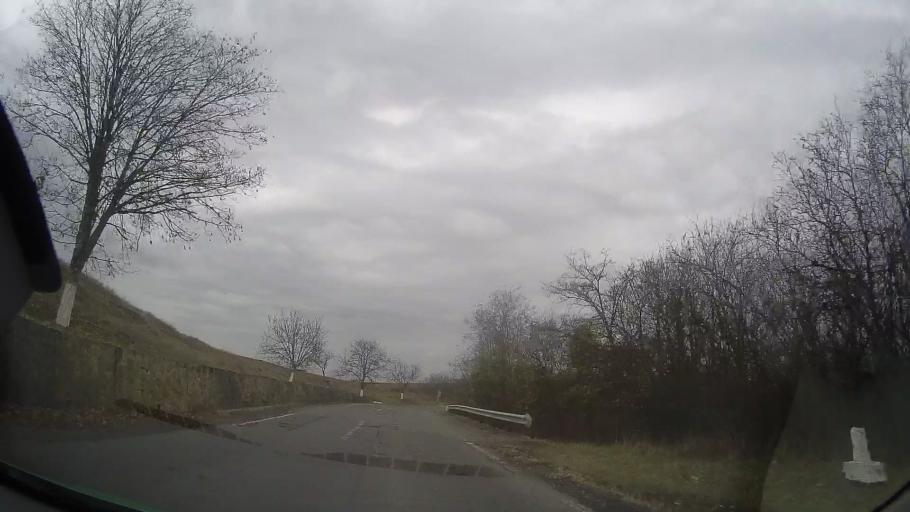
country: RO
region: Mures
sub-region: Comuna Faragau
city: Faragau
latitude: 46.7645
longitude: 24.5300
